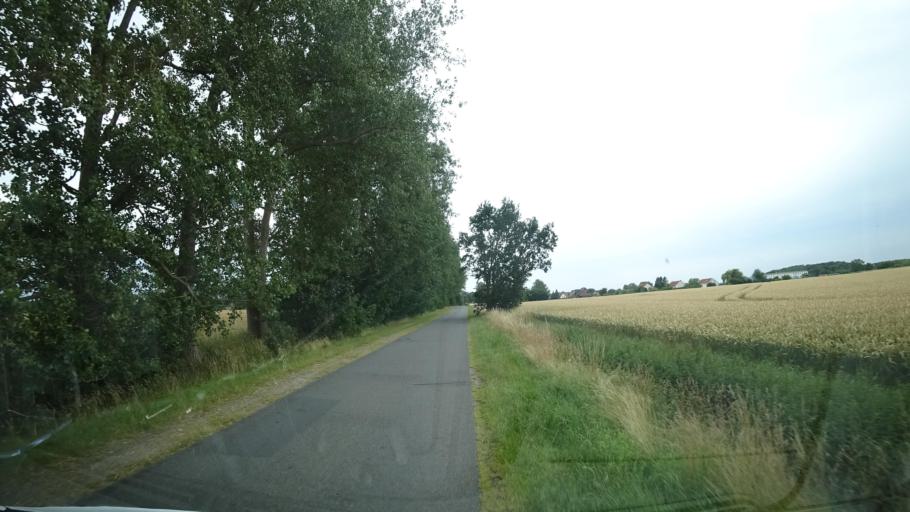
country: DE
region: Mecklenburg-Vorpommern
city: Rambin
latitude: 54.3089
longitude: 13.2111
